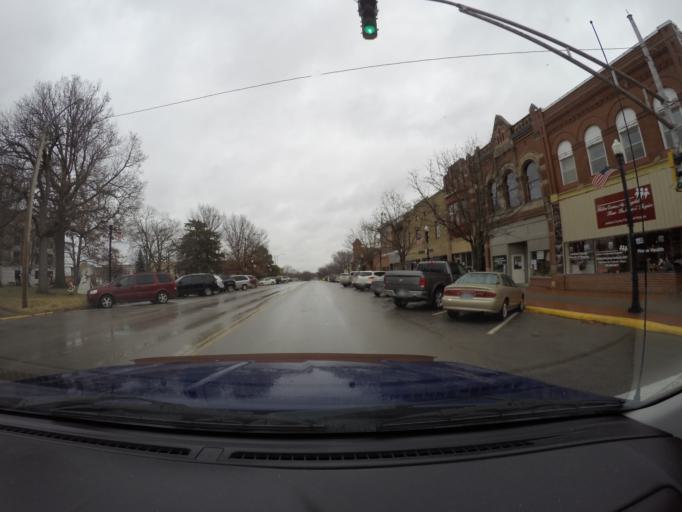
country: US
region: Kansas
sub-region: Jackson County
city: Holton
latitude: 39.4635
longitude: -95.7362
